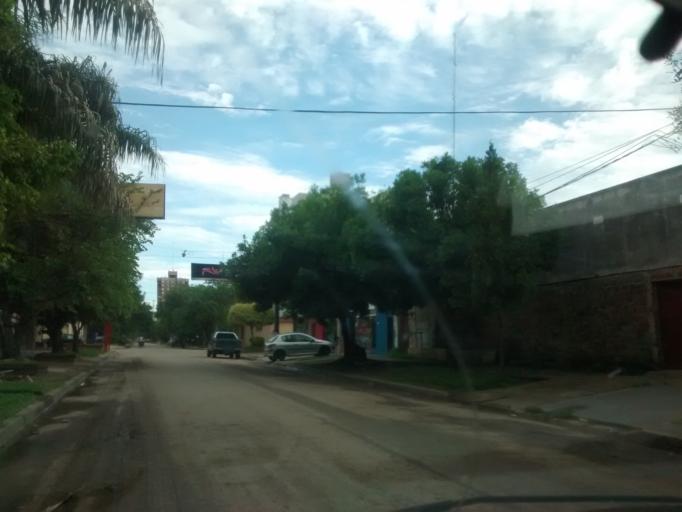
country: AR
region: Chaco
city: Resistencia
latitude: -27.4461
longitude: -58.9940
